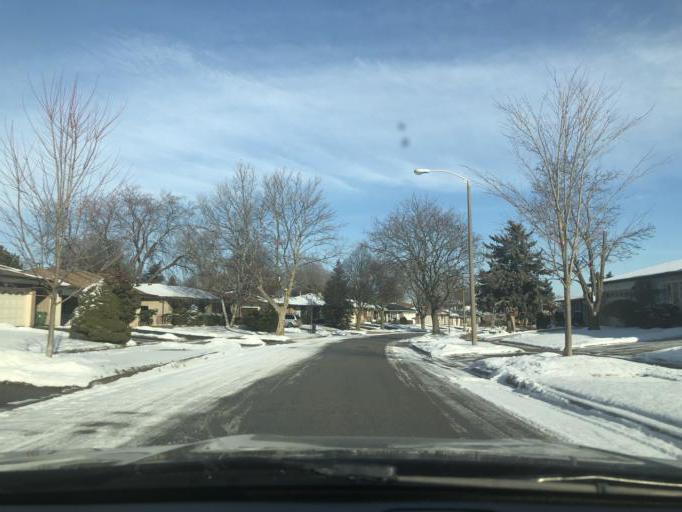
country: CA
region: Ontario
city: Scarborough
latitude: 43.7834
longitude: -79.1427
